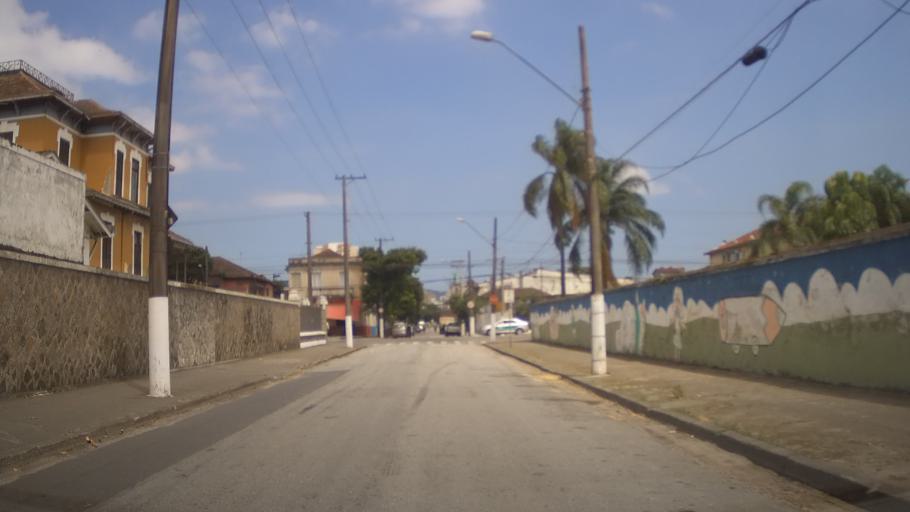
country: BR
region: Sao Paulo
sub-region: Santos
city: Santos
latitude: -23.9560
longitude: -46.3120
